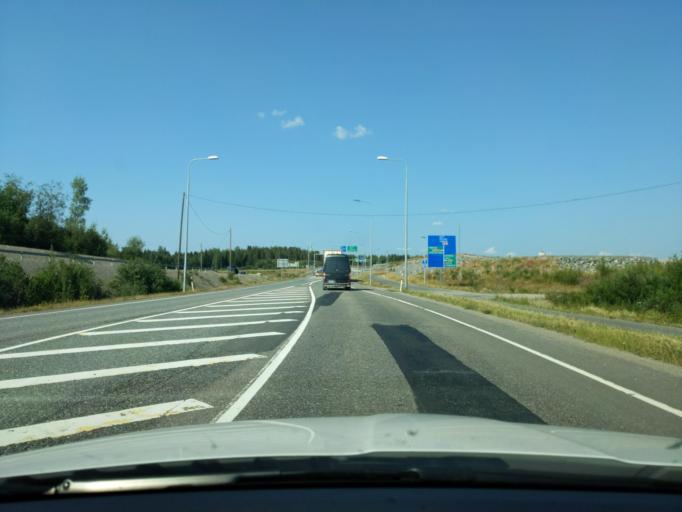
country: FI
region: Paijanne Tavastia
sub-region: Lahti
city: Hollola
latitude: 60.9767
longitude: 25.4826
